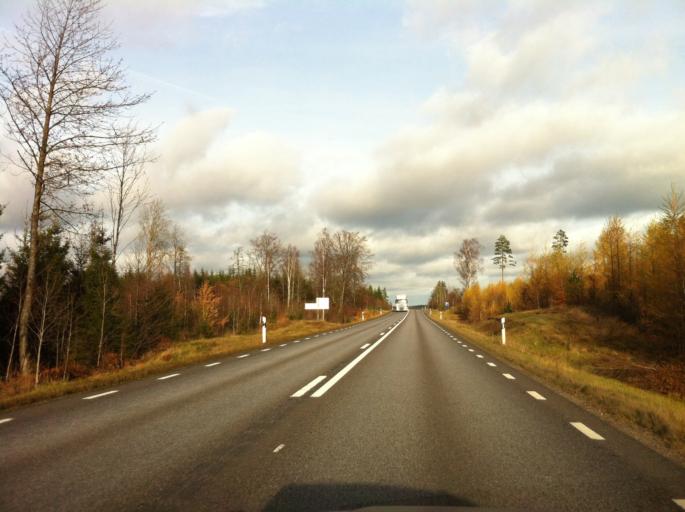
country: SE
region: Kronoberg
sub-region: Vaxjo Kommun
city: Gemla
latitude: 56.7796
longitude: 14.5686
